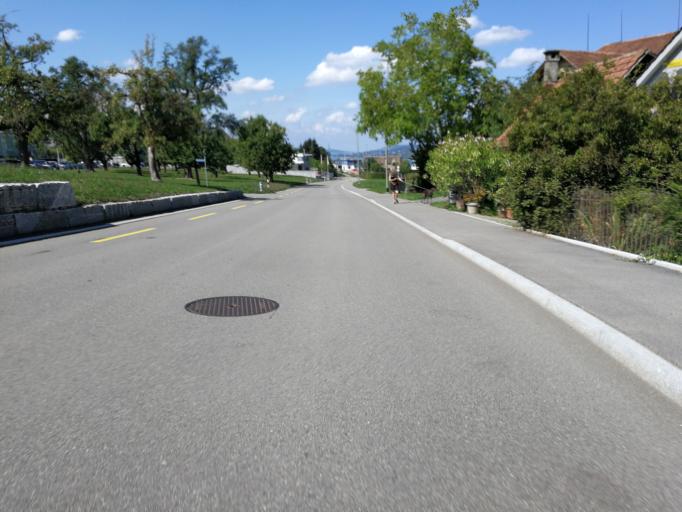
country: CH
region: Zurich
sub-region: Bezirk Horgen
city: Horgen / Allmend
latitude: 47.2491
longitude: 8.6193
